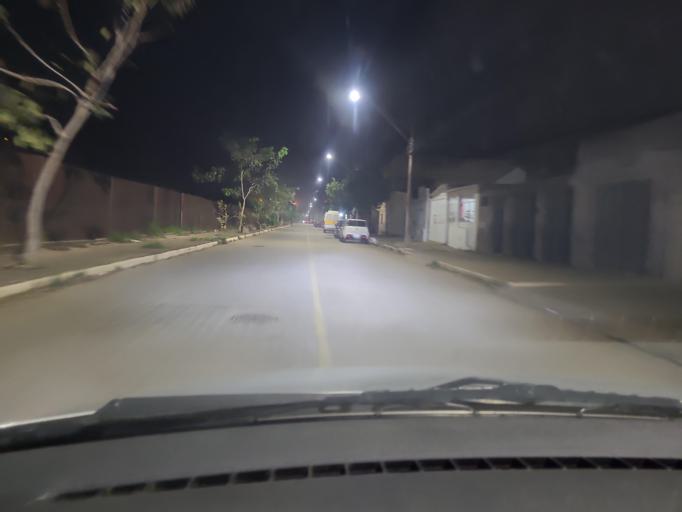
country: BR
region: Minas Gerais
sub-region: Governador Valadares
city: Governador Valadares
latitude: -18.8773
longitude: -41.9670
